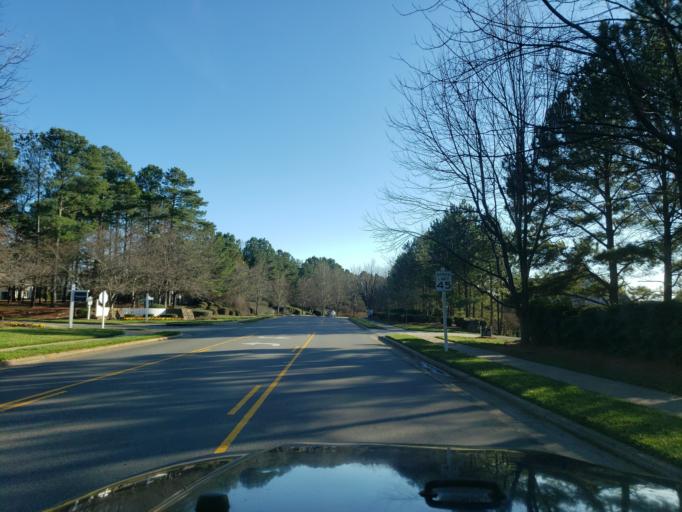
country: US
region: North Carolina
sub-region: Catawba County
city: Lake Norman of Catawba
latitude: 35.5403
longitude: -80.9170
